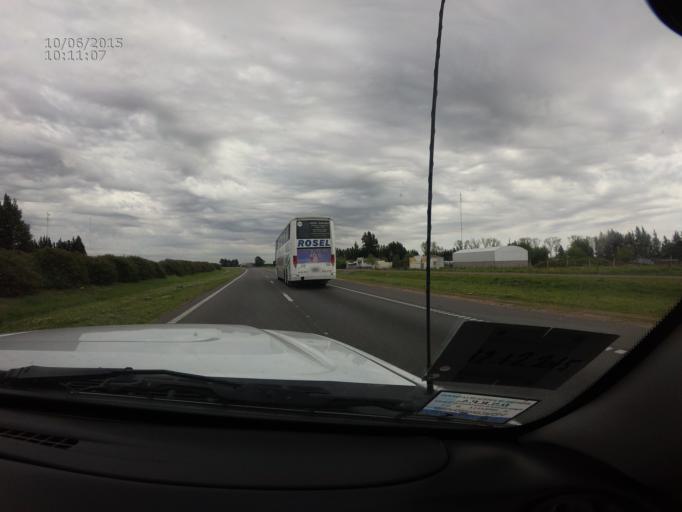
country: AR
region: Buenos Aires
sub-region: Partido de San Pedro
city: San Pedro
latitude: -33.7780
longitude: -59.6490
